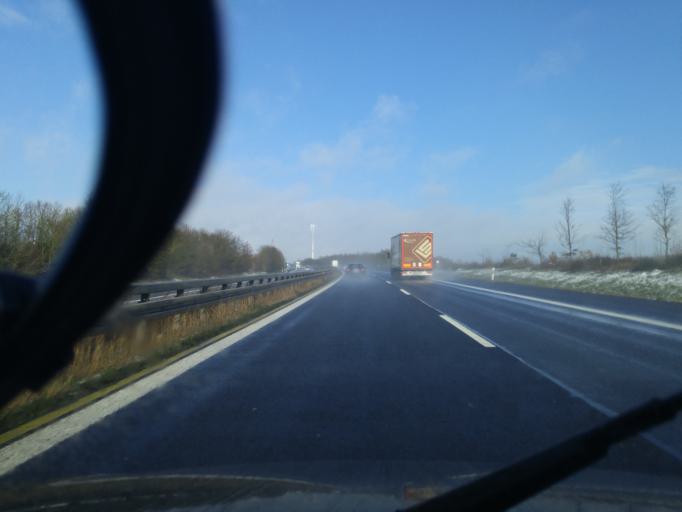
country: DE
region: Bavaria
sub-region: Regierungsbezirk Unterfranken
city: Werneck
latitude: 50.0244
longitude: 10.0696
